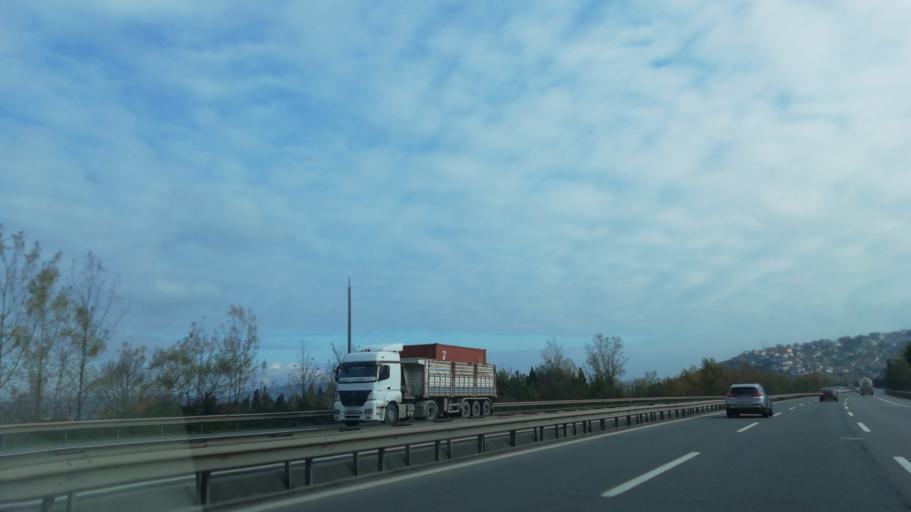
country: TR
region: Sakarya
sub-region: Merkez
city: Sapanca
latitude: 40.6871
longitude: 30.2752
